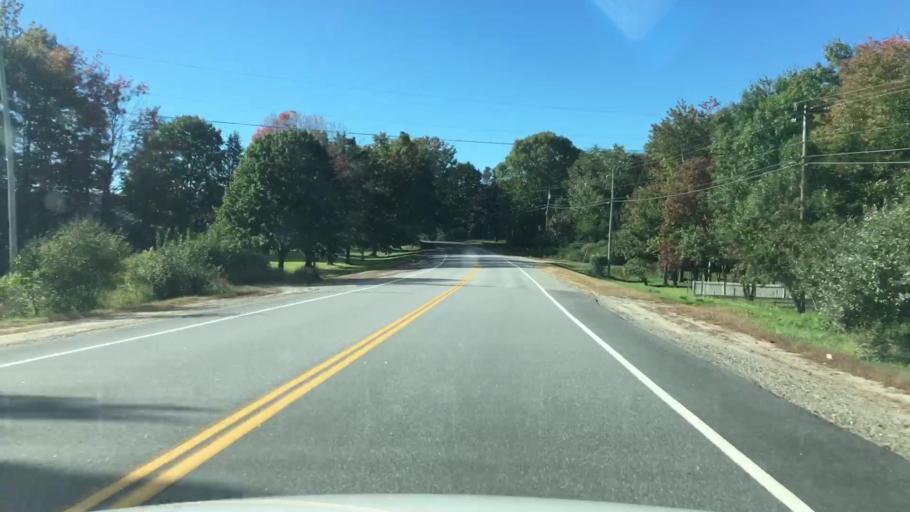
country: US
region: Maine
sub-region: Sagadahoc County
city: Topsham
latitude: 43.9292
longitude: -70.0018
